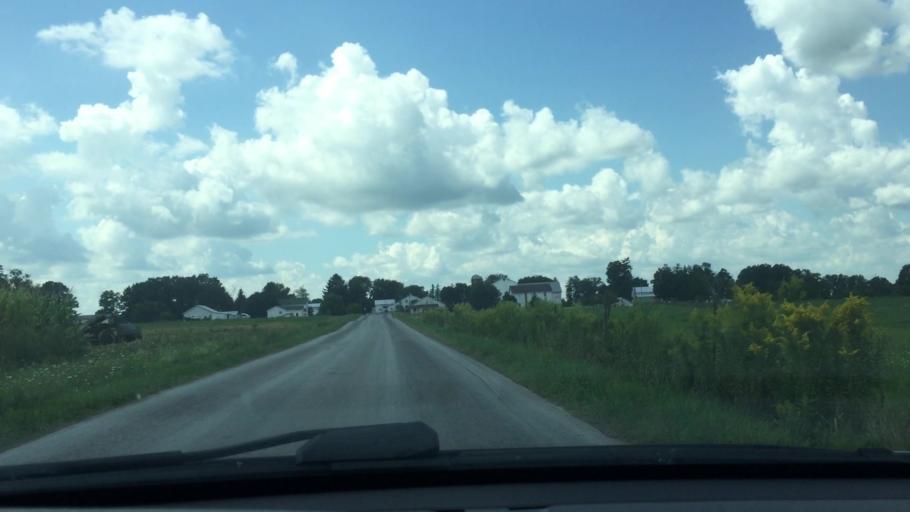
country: US
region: Pennsylvania
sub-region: Lawrence County
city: New Wilmington
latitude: 41.1154
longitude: -80.3555
